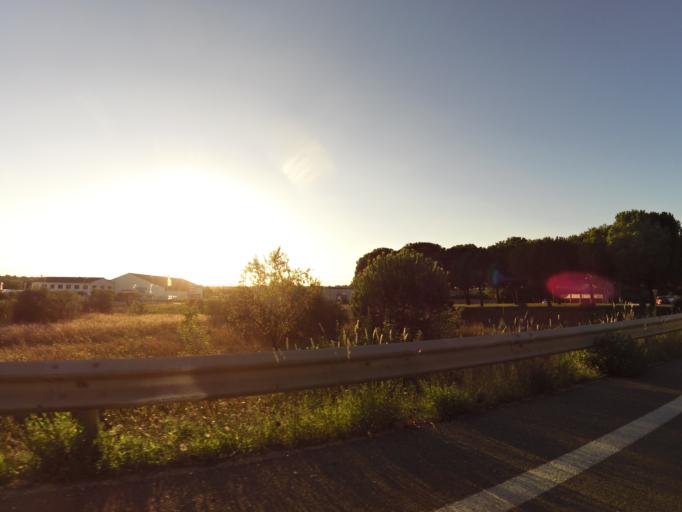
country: FR
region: Languedoc-Roussillon
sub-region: Departement du Gard
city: Milhaud
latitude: 43.7993
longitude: 4.3173
